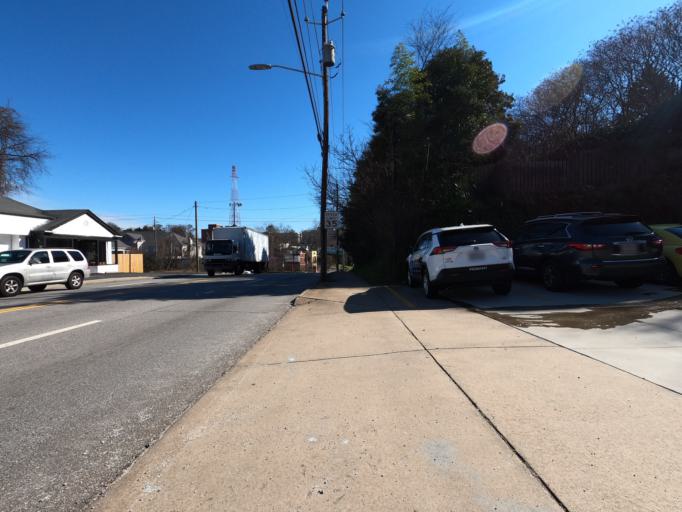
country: US
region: Georgia
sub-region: Clarke County
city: Athens
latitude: 33.9560
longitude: -83.3836
